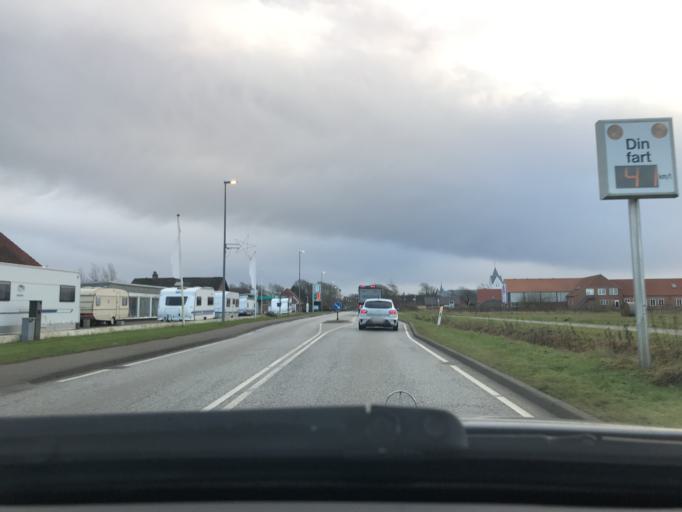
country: DK
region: South Denmark
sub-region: Tonder Kommune
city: Sherrebek
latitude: 55.1971
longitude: 8.7270
